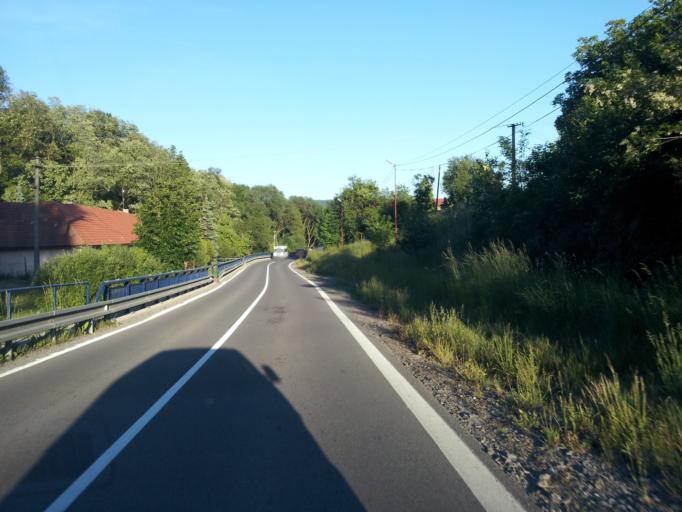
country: SK
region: Banskobystricky
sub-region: Okres Banska Bystrica
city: Banska Stiavnica
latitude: 48.4412
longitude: 18.9162
